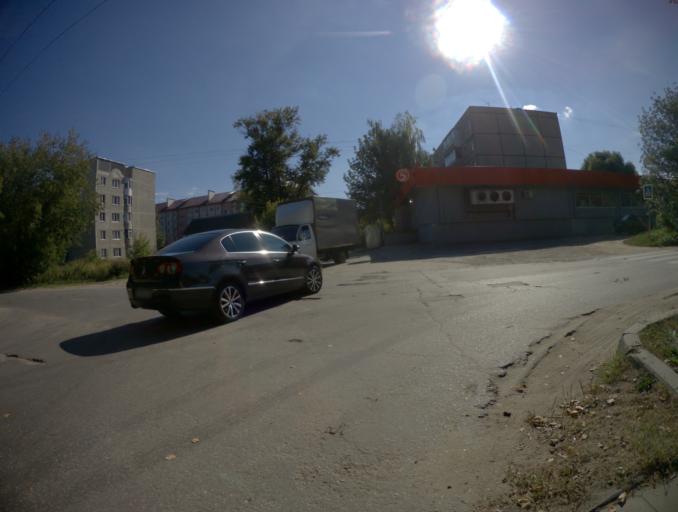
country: RU
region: Vladimir
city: Gus'-Khrustal'nyy
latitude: 55.6157
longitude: 40.6560
